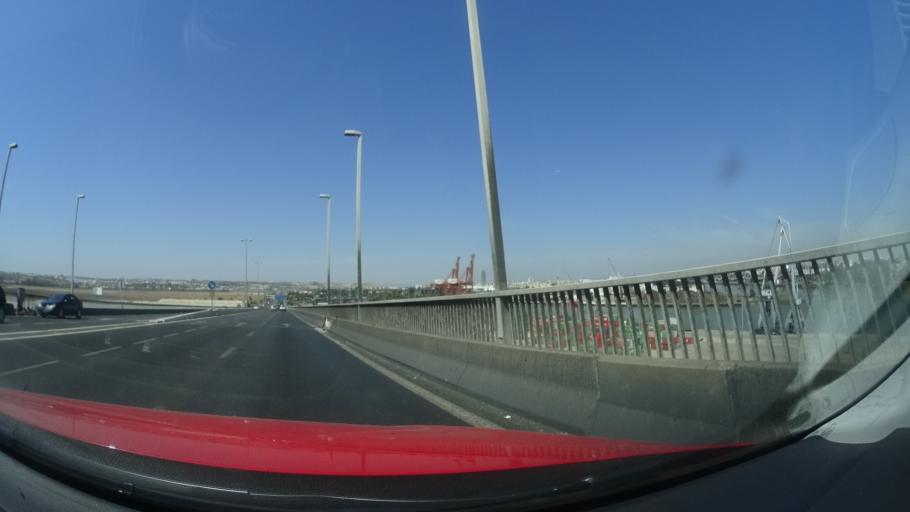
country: ES
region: Andalusia
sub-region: Provincia de Sevilla
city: Gelves
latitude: 37.3518
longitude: -5.9963
